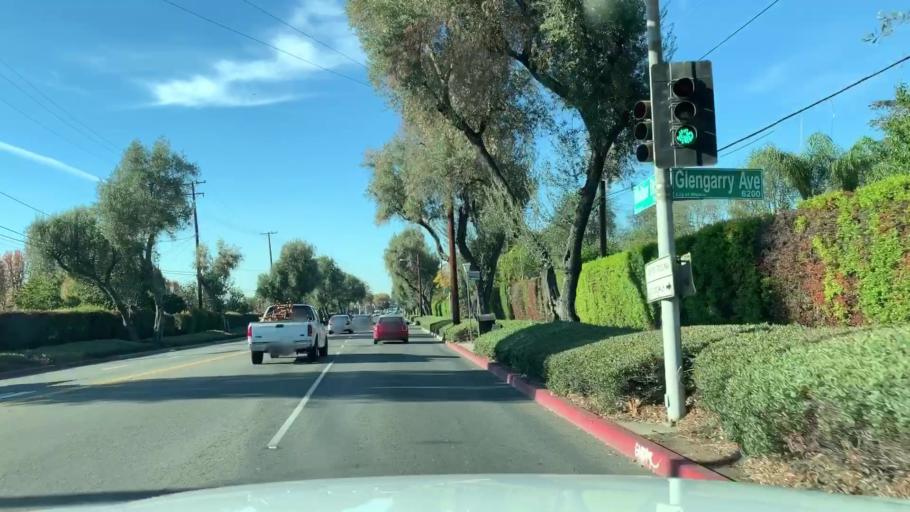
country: US
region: California
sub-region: Los Angeles County
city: West Whittier-Los Nietos
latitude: 33.9876
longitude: -118.0605
